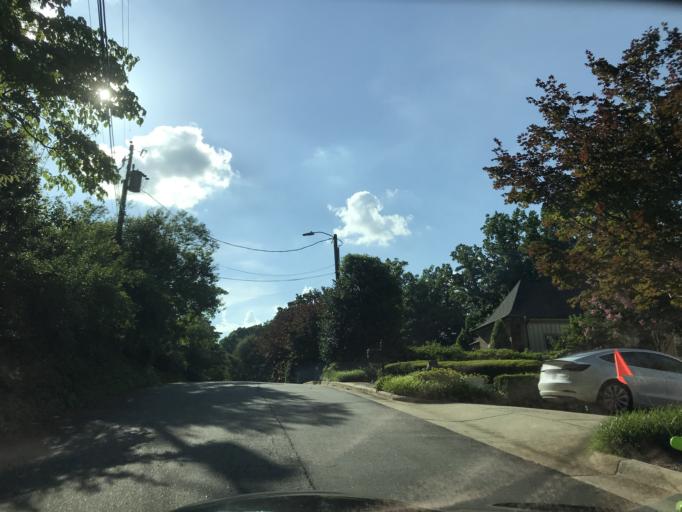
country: US
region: North Carolina
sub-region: Wake County
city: West Raleigh
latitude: 35.8088
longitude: -78.6649
